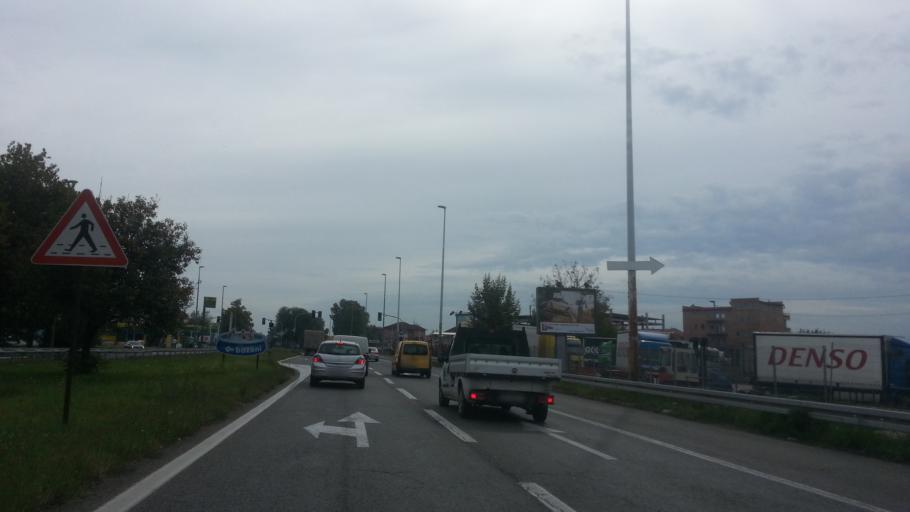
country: RS
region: Central Serbia
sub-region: Belgrade
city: Zemun
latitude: 44.8537
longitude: 20.3672
